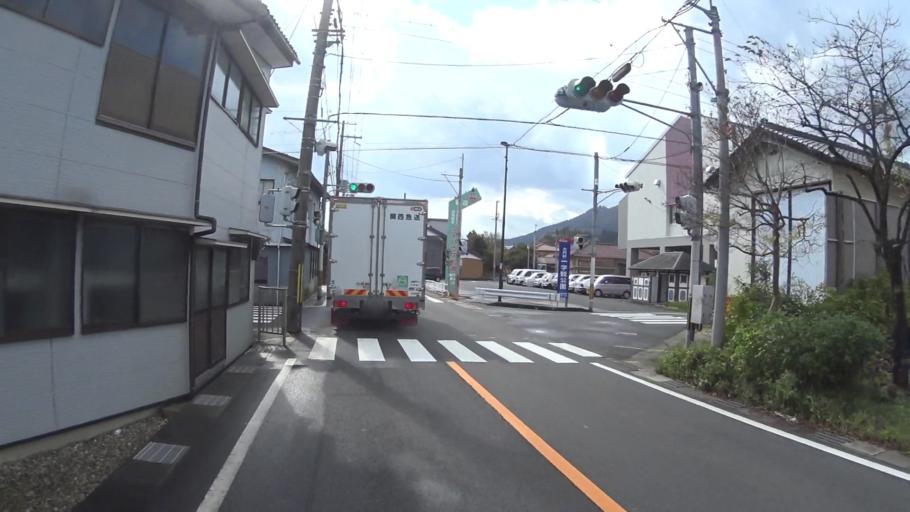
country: JP
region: Kyoto
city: Miyazu
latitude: 35.5692
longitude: 135.1550
